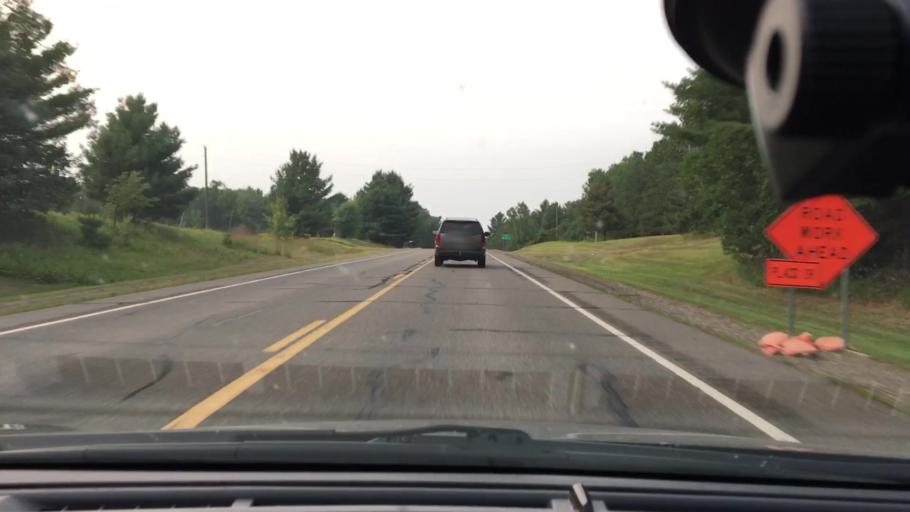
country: US
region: Minnesota
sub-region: Crow Wing County
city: Crosby
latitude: 46.4147
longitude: -93.8727
